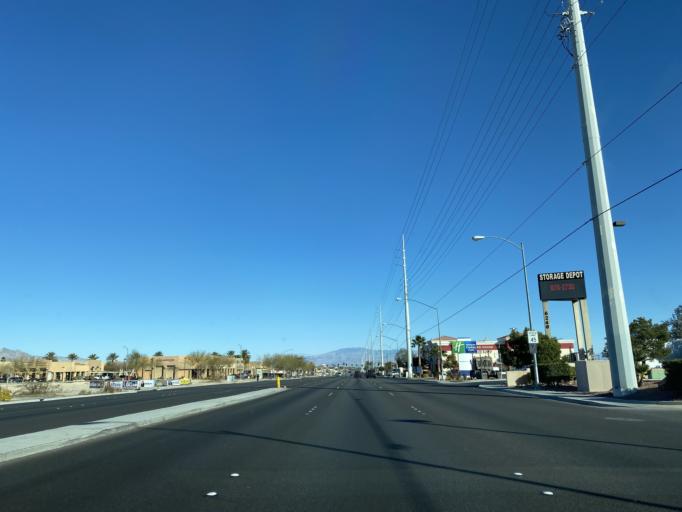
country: US
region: Nevada
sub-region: Clark County
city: Spring Valley
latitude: 36.0747
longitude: -115.2425
